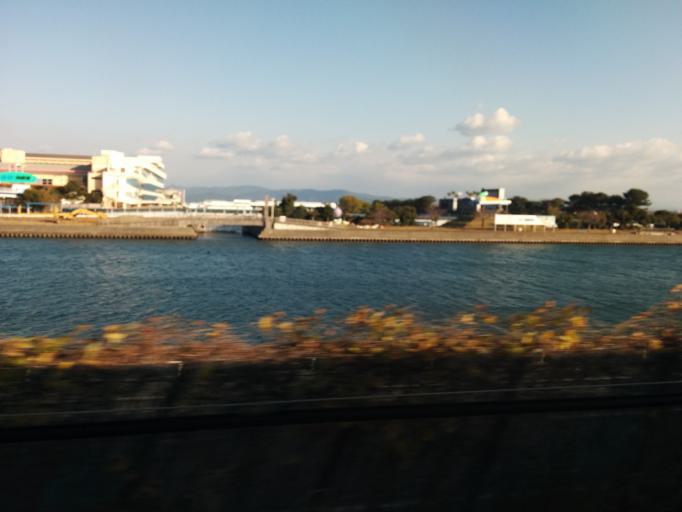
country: JP
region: Shizuoka
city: Kosai-shi
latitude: 34.6947
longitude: 137.5725
